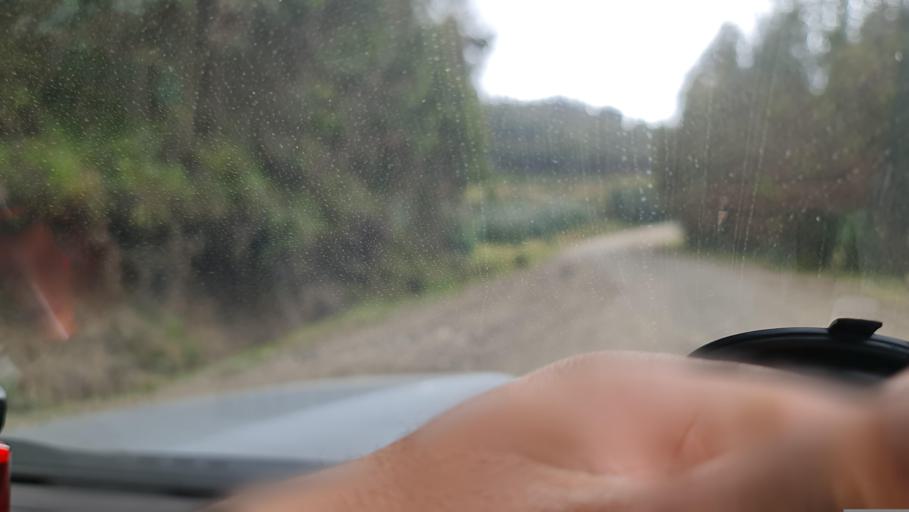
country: ET
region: Amhara
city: Abomsa
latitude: 10.1336
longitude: 39.7900
